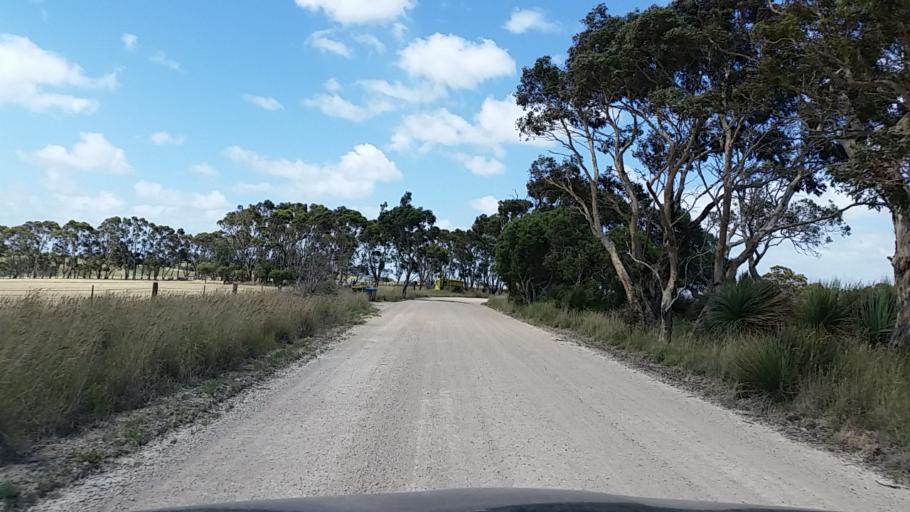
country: AU
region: South Australia
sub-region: Alexandrina
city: Port Elliot
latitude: -35.4499
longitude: 138.6486
